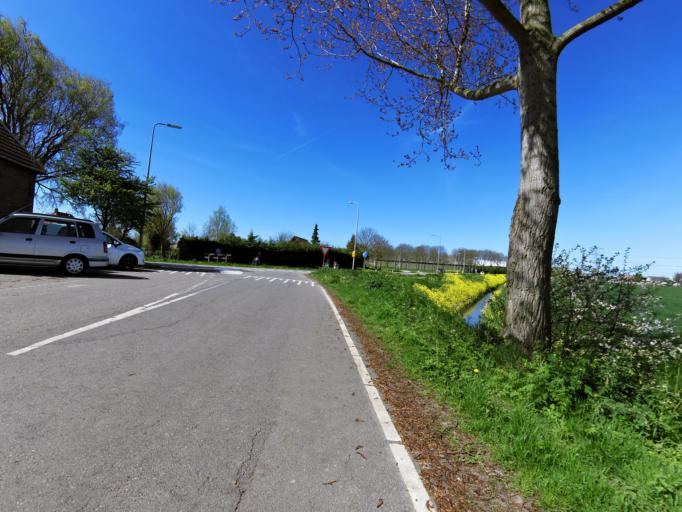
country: NL
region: South Holland
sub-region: Gemeente Brielle
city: Brielle
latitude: 51.8908
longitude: 4.1424
